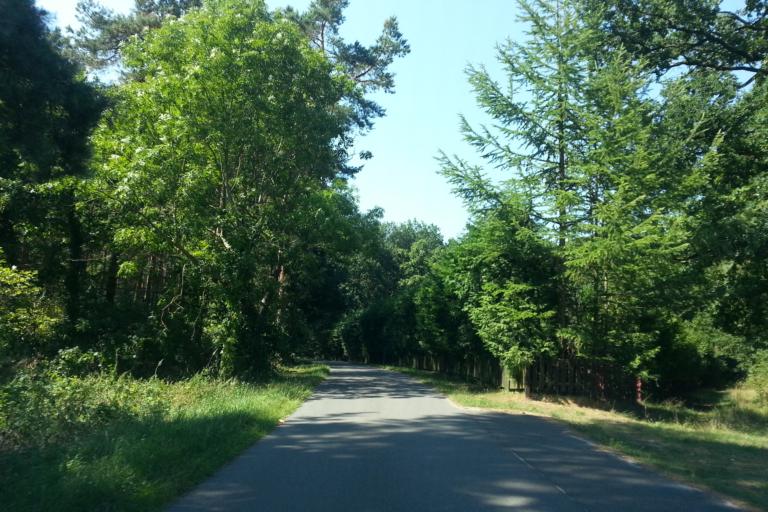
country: DE
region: Mecklenburg-Vorpommern
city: Ferdinandshof
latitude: 53.7064
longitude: 13.8323
